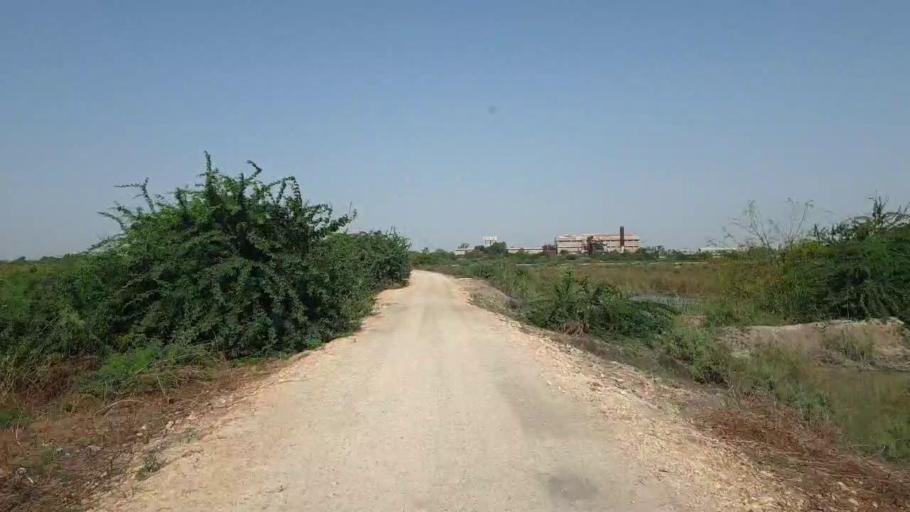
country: PK
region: Sindh
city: Tando Bago
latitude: 24.7386
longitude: 69.0746
